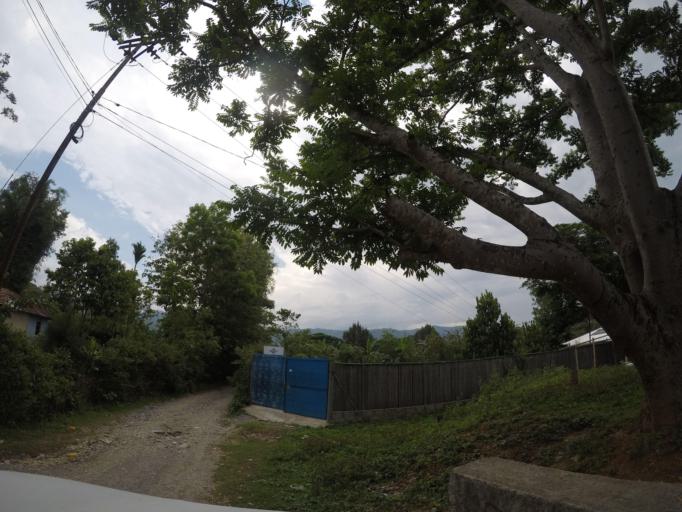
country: TL
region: Ermera
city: Gleno
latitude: -8.7131
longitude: 125.4420
